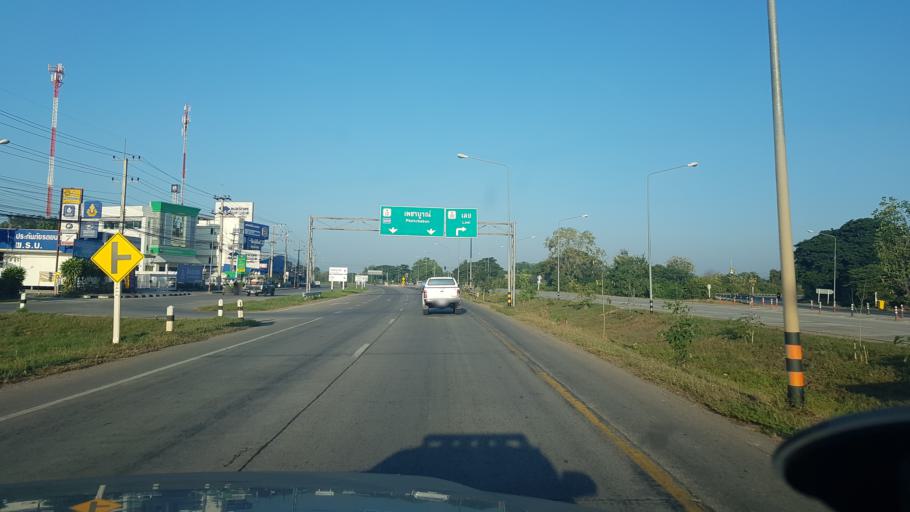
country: TH
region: Chaiyaphum
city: Khon San
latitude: 16.5887
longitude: 102.0000
